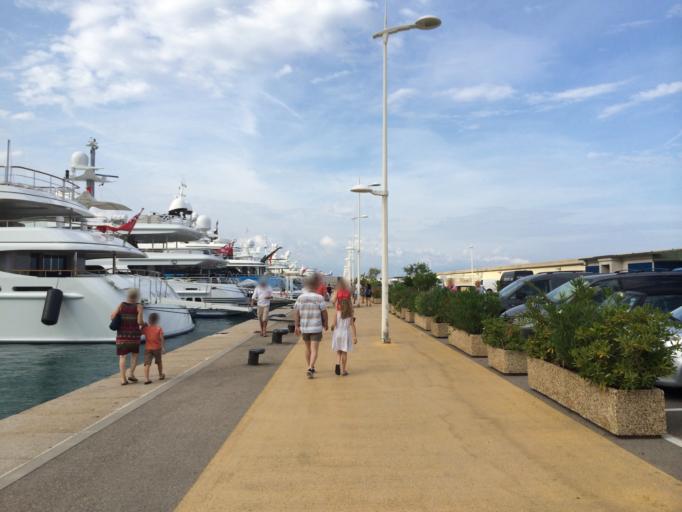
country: FR
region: Provence-Alpes-Cote d'Azur
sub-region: Departement des Alpes-Maritimes
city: Antibes
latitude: 43.5855
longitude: 7.1299
